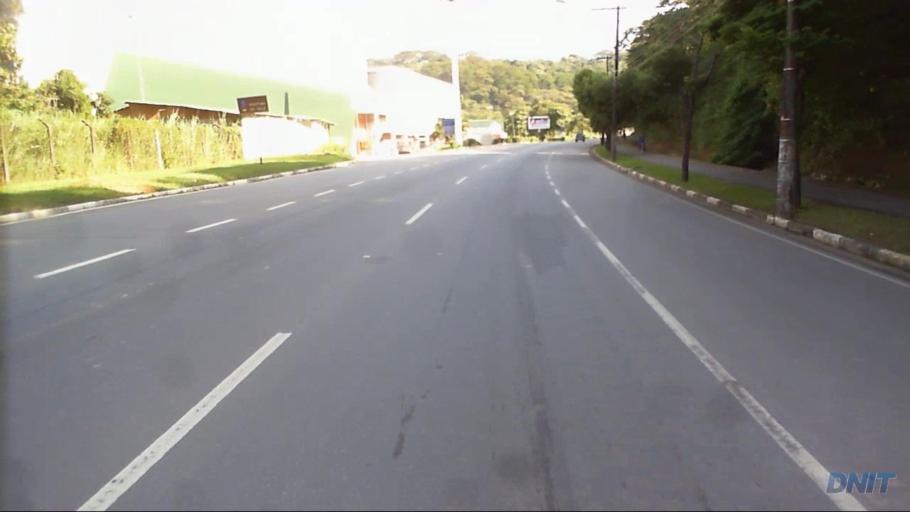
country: BR
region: Minas Gerais
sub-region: Ipatinga
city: Ipatinga
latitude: -19.4943
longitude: -42.5652
